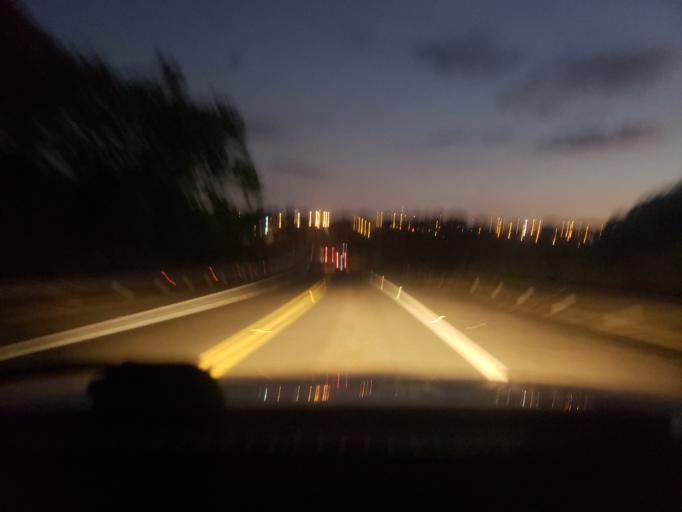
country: BR
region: Sao Paulo
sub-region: Conchal
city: Conchal
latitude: -22.3346
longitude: -47.1557
